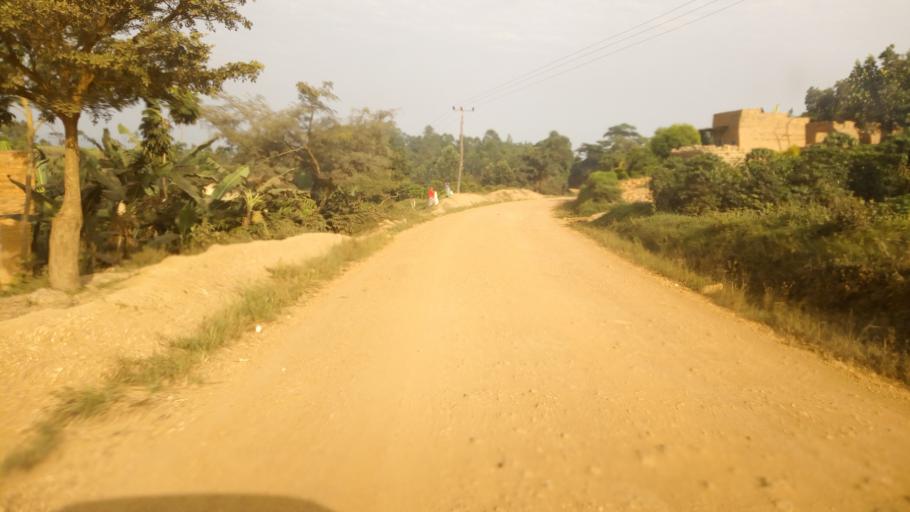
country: UG
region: Western Region
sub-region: Kanungu District
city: Ntungamo
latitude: -0.8352
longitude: 29.6741
